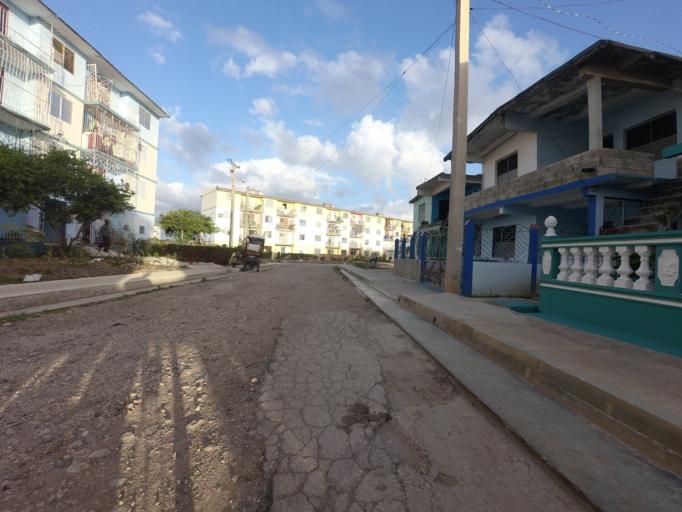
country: CU
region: Ciego de Avila
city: Ciego de Avila
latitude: 21.8439
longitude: -78.7485
